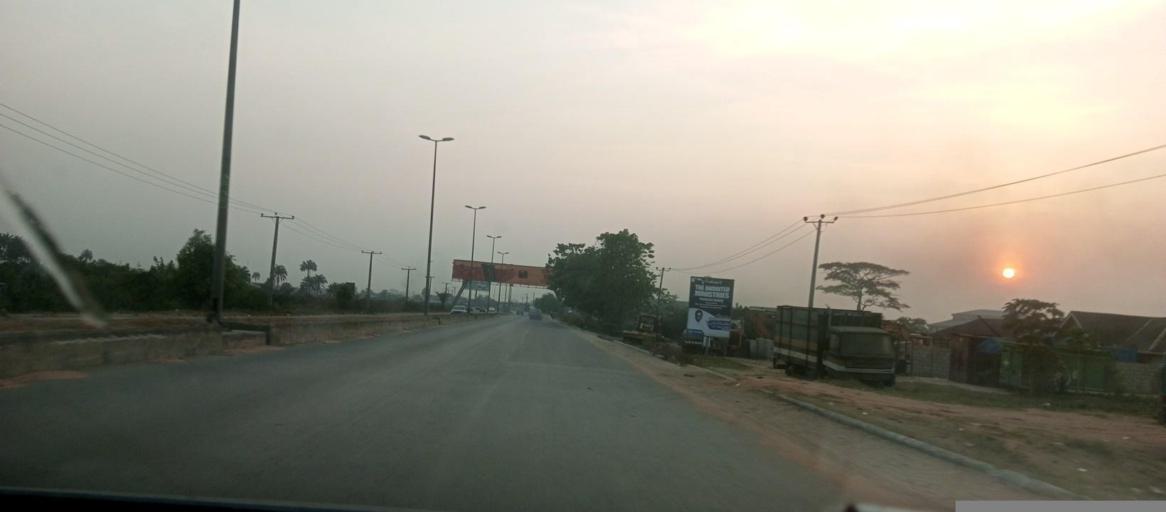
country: NG
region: Rivers
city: Emuoha
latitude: 4.9301
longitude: 7.0015
